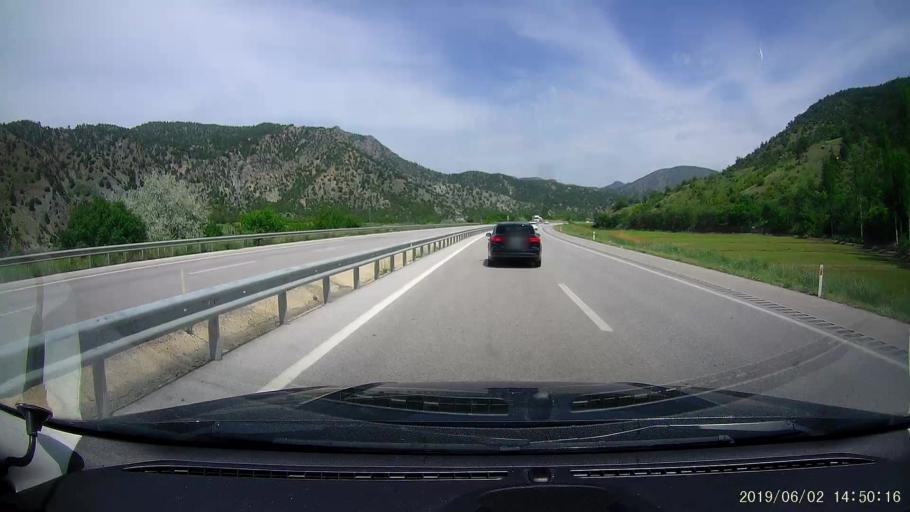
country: TR
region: Corum
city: Hacihamza
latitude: 41.0724
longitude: 34.5149
